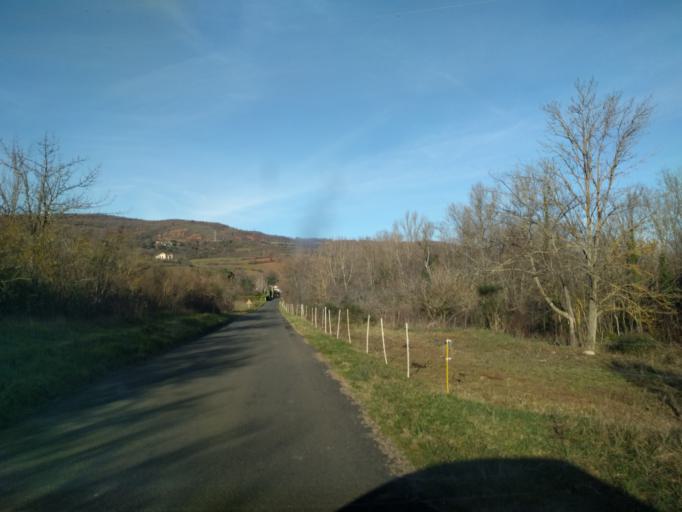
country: FR
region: Languedoc-Roussillon
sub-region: Departement de l'Aude
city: Quillan
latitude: 42.9018
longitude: 2.1875
